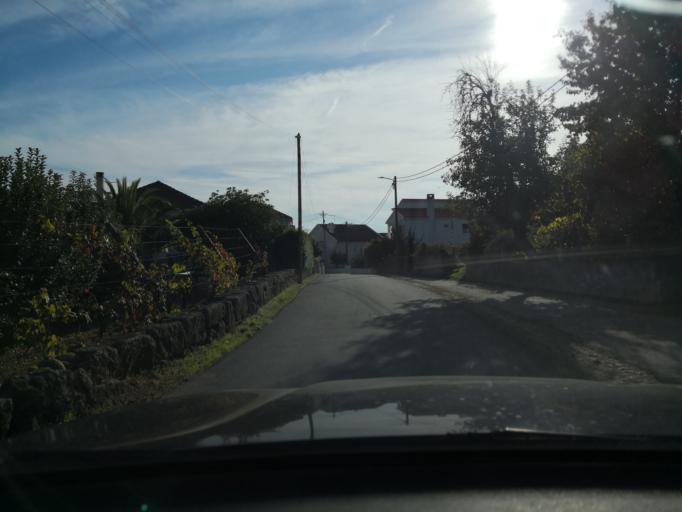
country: PT
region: Vila Real
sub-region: Vila Real
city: Vila Real
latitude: 41.3254
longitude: -7.7409
